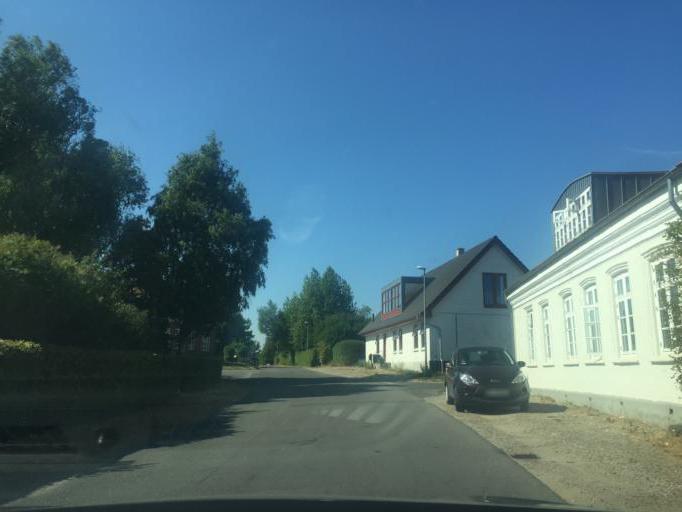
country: DK
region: Central Jutland
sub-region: Hedensted Kommune
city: Juelsminde
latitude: 55.7064
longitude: 9.9806
